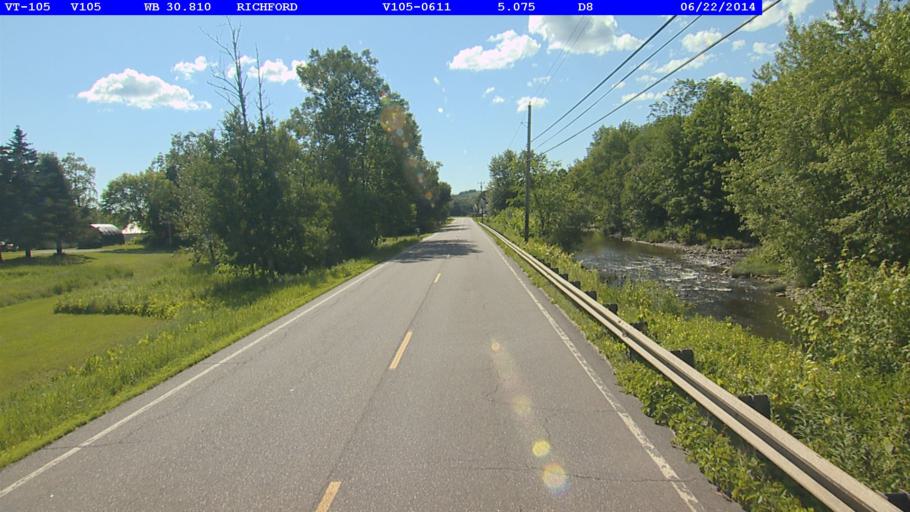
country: US
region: Vermont
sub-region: Franklin County
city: Richford
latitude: 44.9955
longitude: -72.6197
